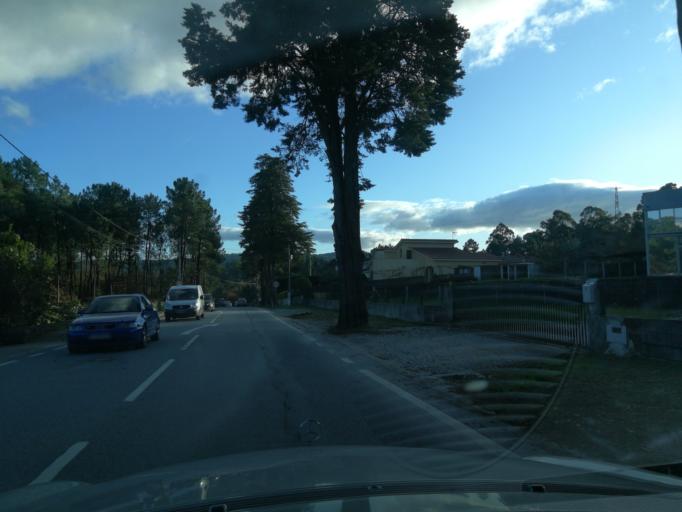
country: PT
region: Viana do Castelo
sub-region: Viana do Castelo
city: Darque
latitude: 41.6191
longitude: -8.7556
